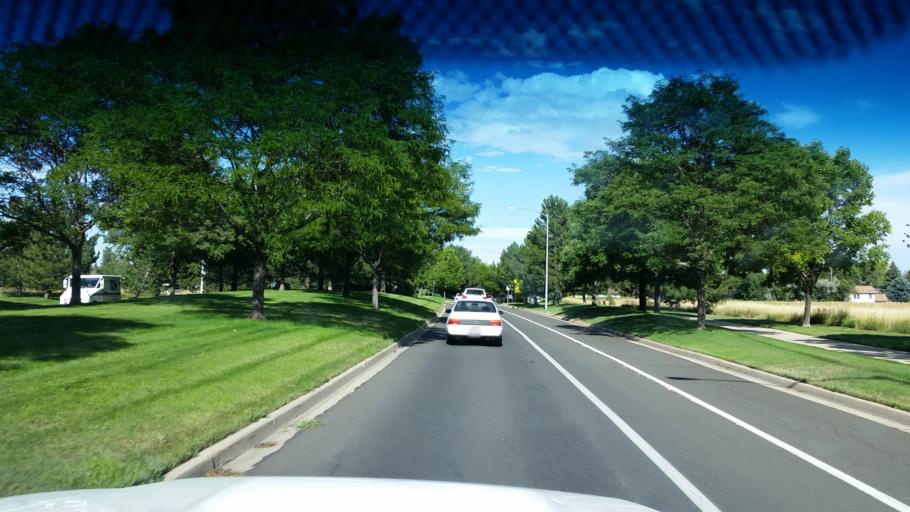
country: US
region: Colorado
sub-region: Broomfield County
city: Broomfield
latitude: 39.9248
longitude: -105.0650
